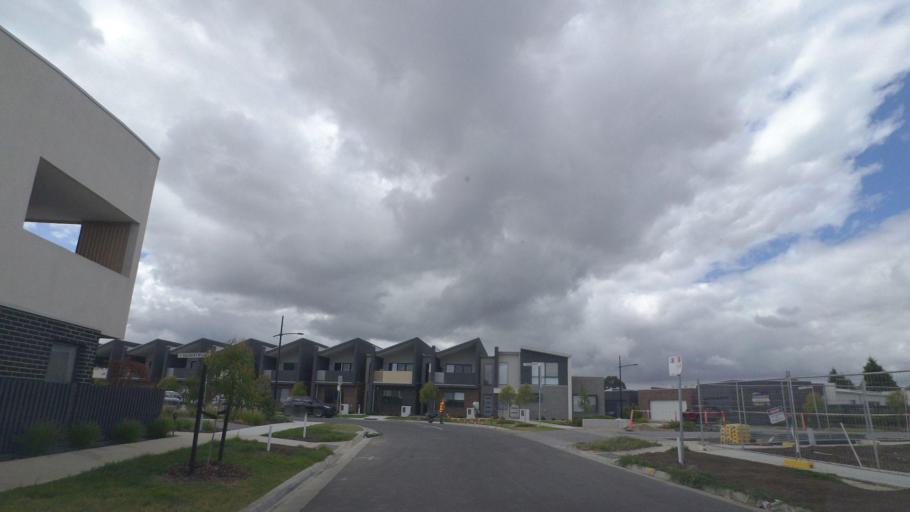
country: AU
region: Victoria
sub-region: Knox
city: Scoresby
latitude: -37.9151
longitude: 145.2299
